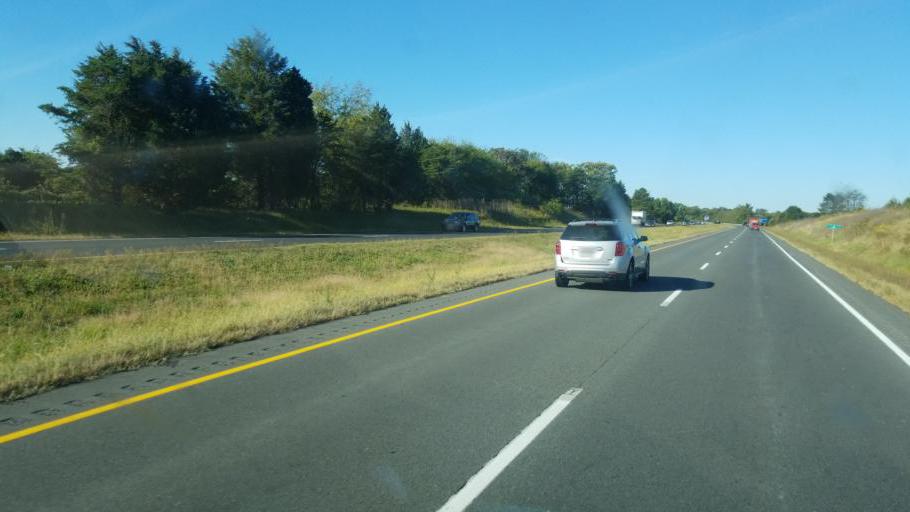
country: US
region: Virginia
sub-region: Culpeper County
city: Culpeper
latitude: 38.4994
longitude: -77.9207
